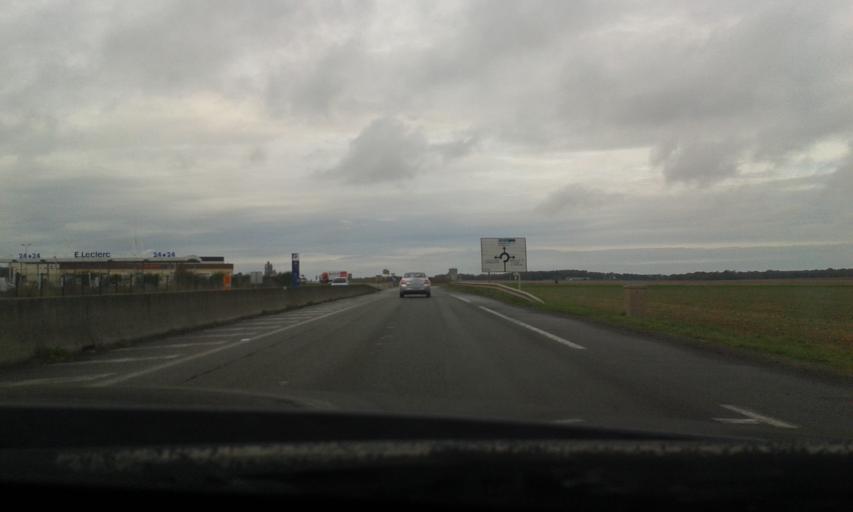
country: FR
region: Centre
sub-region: Departement d'Eure-et-Loir
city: Saint-Lubin-des-Joncherets
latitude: 48.7746
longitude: 1.2127
